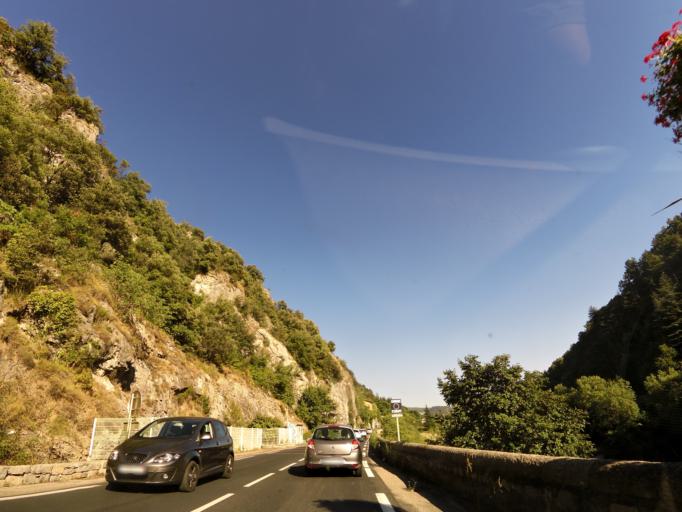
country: FR
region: Languedoc-Roussillon
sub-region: Departement de l'Herault
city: Ganges
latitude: 43.9381
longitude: 3.6935
